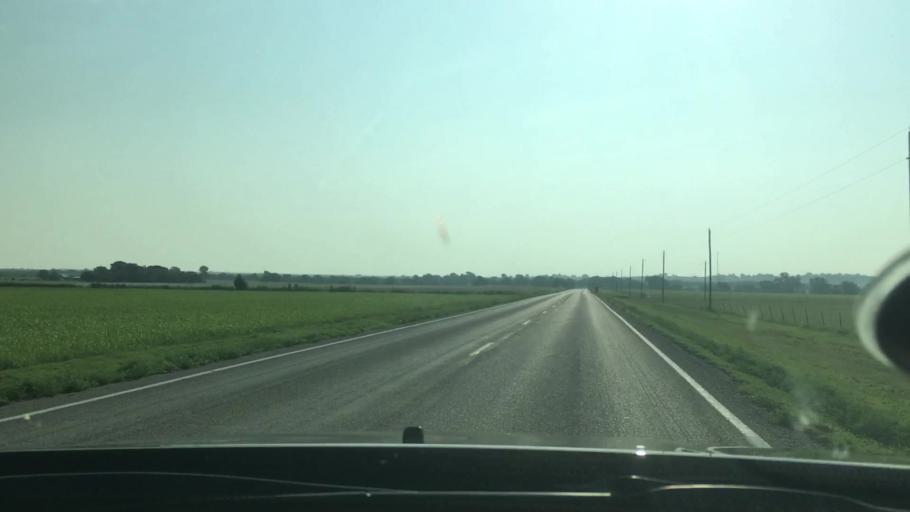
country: US
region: Oklahoma
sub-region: Bryan County
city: Durant
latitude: 34.1426
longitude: -96.2974
